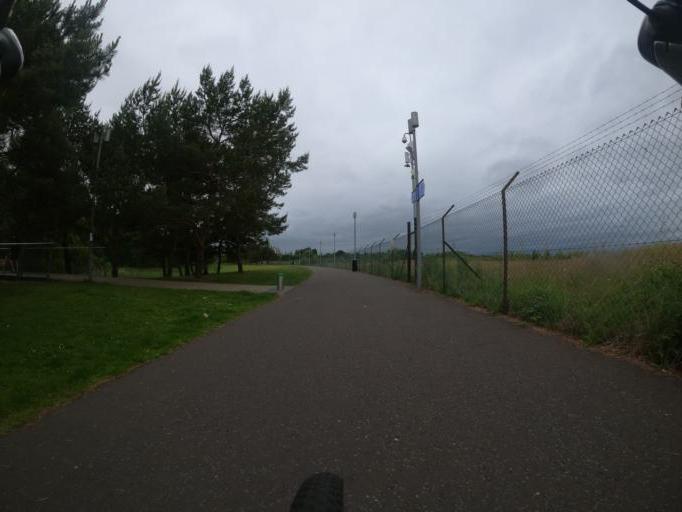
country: GB
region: Scotland
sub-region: Edinburgh
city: Edinburgh
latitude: 55.9791
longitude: -3.2445
